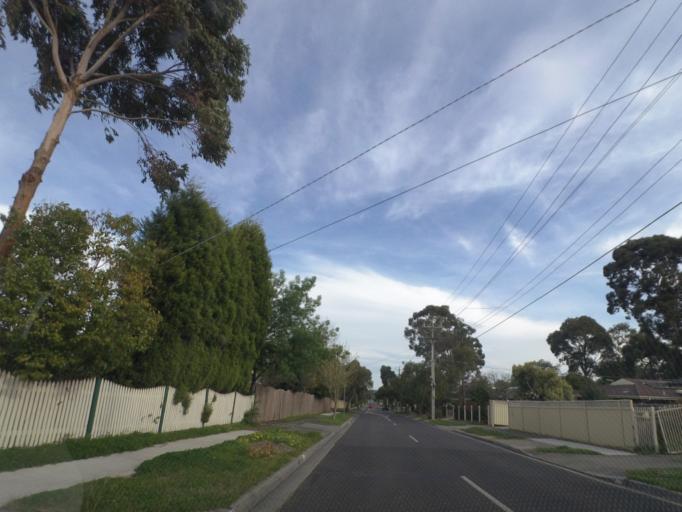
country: AU
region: Victoria
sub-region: Knox
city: Knoxfield
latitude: -37.8878
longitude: 145.2405
